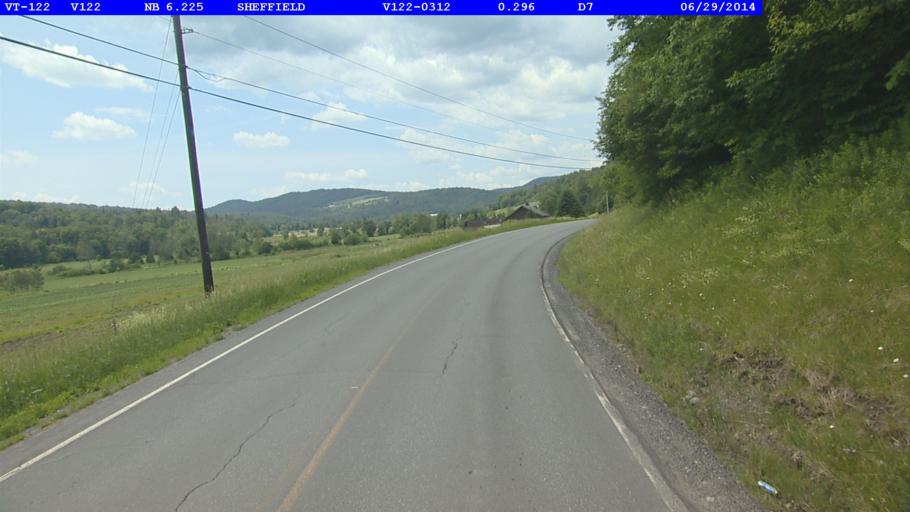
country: US
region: Vermont
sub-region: Caledonia County
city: Lyndonville
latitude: 44.5931
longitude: -72.0964
